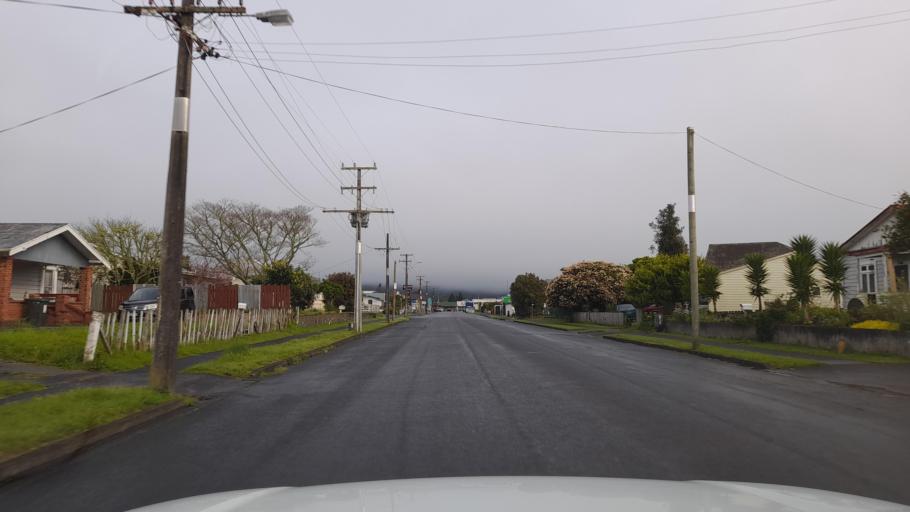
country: NZ
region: Northland
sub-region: Far North District
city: Waimate North
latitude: -35.4099
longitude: 173.8028
